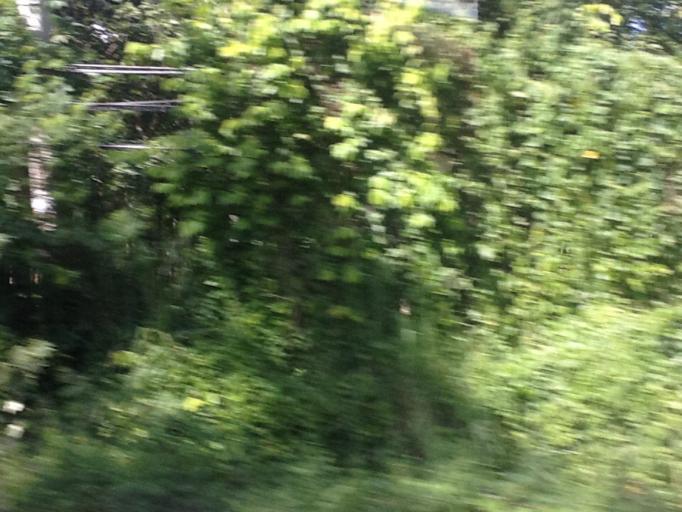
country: TH
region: Phuket
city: Thalang
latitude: 8.1243
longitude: 98.3192
